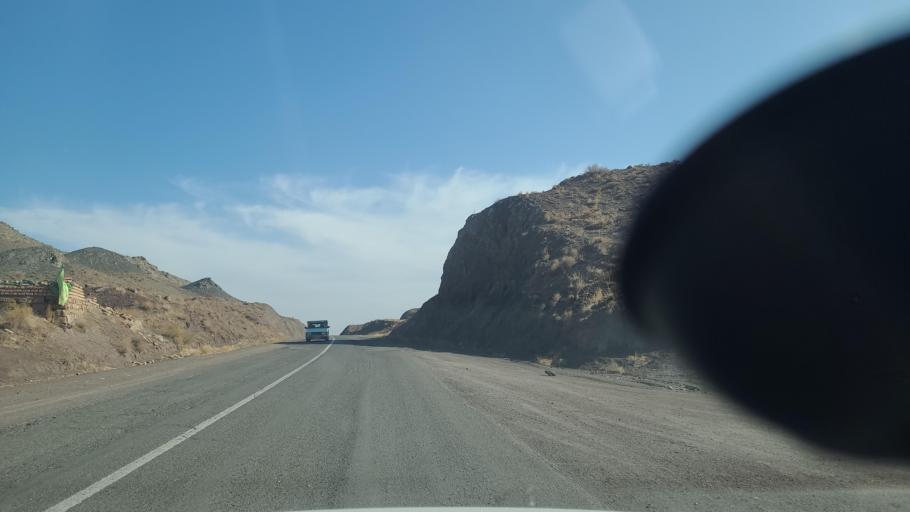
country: IR
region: Razavi Khorasan
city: Fariman
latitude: 35.5942
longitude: 59.7150
